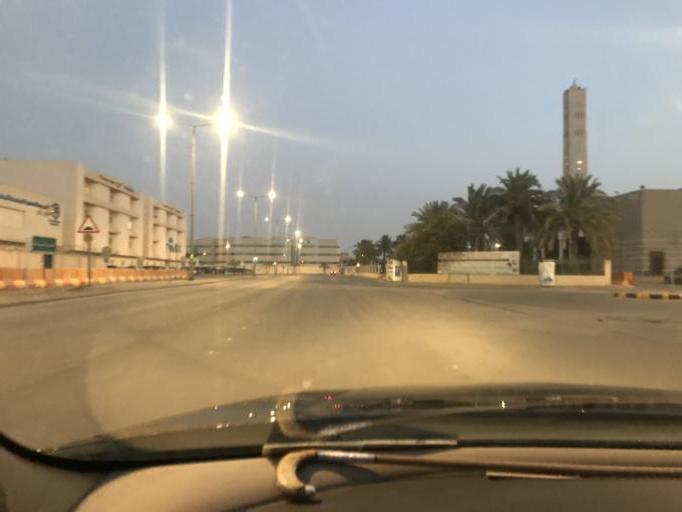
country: SA
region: Ar Riyad
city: Riyadh
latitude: 24.7981
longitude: 46.7090
